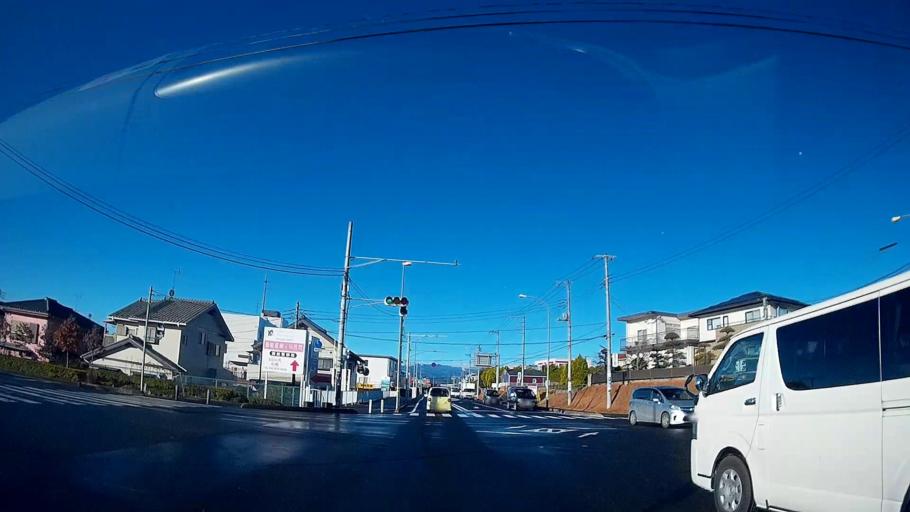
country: JP
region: Saitama
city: Hanno
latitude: 35.8587
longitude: 139.3369
